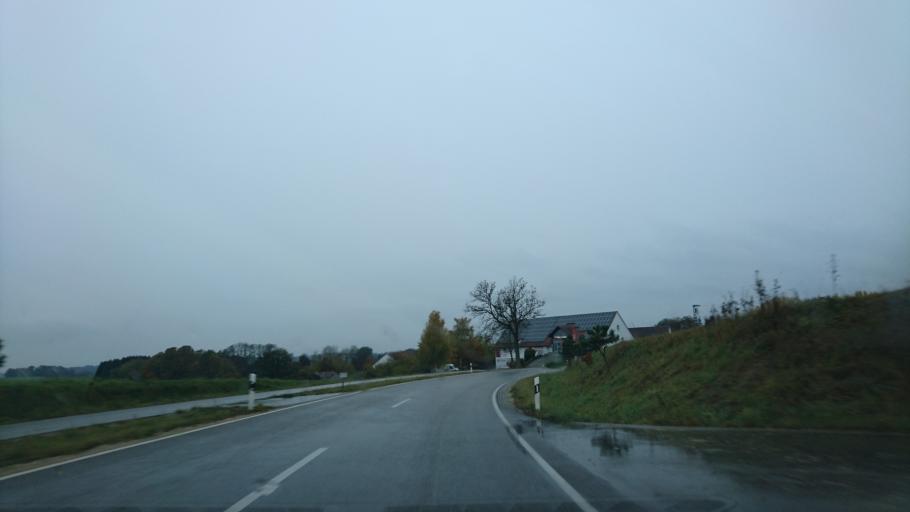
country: DE
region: Bavaria
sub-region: Upper Bavaria
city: Hilgertshausen-Tandern
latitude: 48.4324
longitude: 11.3284
